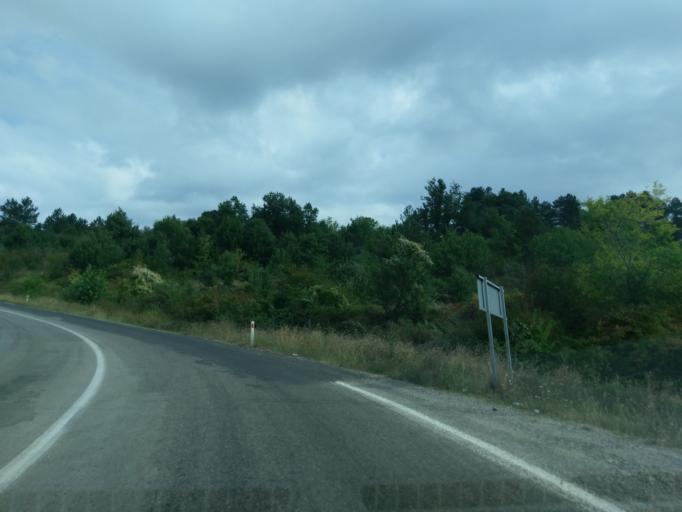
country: TR
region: Sinop
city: Yenikonak
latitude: 41.9391
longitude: 34.7232
